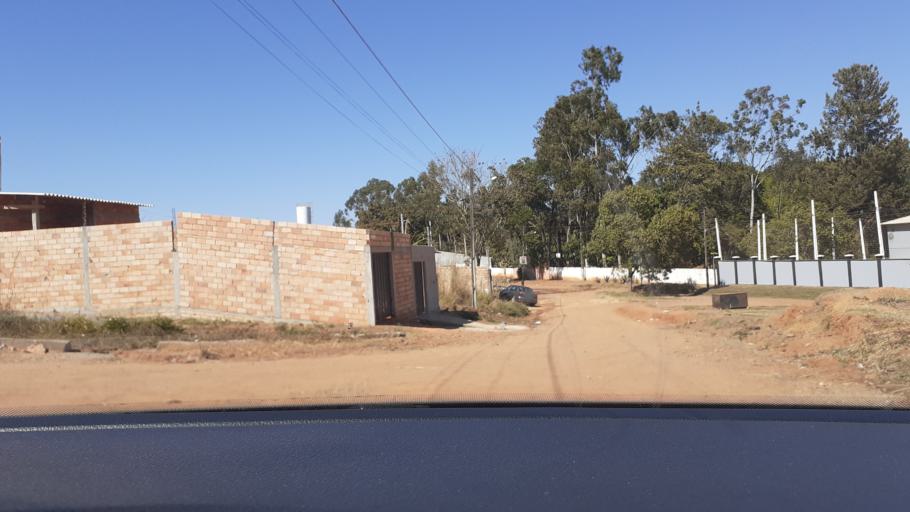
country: BR
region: Goias
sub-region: Aparecida De Goiania
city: Aparecida de Goiania
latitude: -16.8799
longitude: -49.2614
